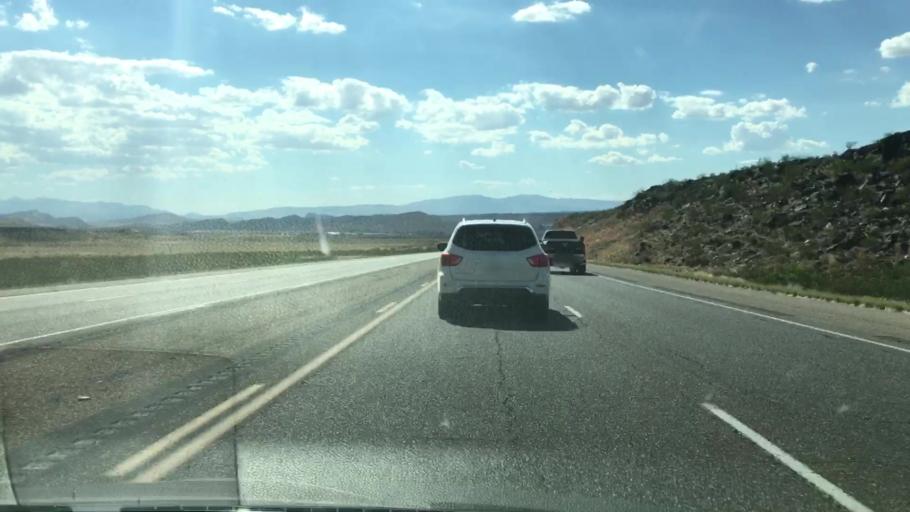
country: US
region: Utah
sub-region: Washington County
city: Hurricane
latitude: 37.1727
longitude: -113.3533
